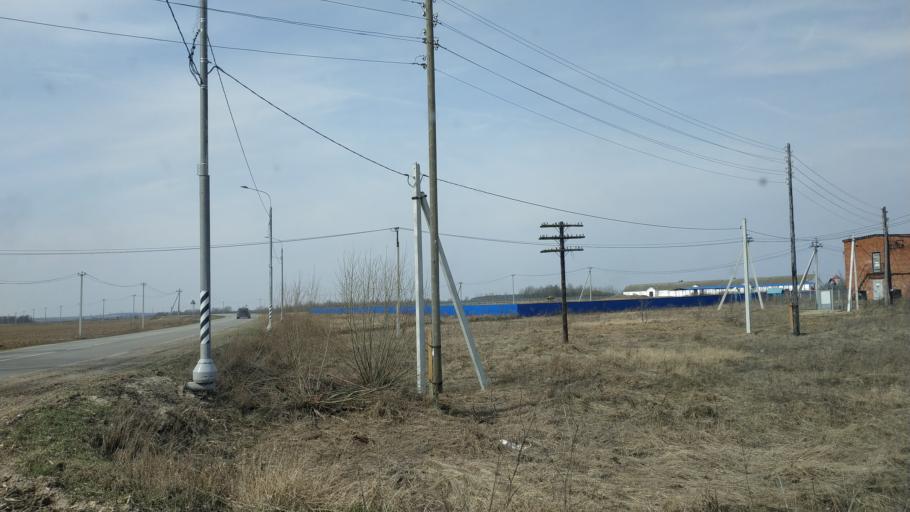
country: RU
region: Moskovskaya
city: Troitskoye
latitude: 55.3601
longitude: 38.5458
